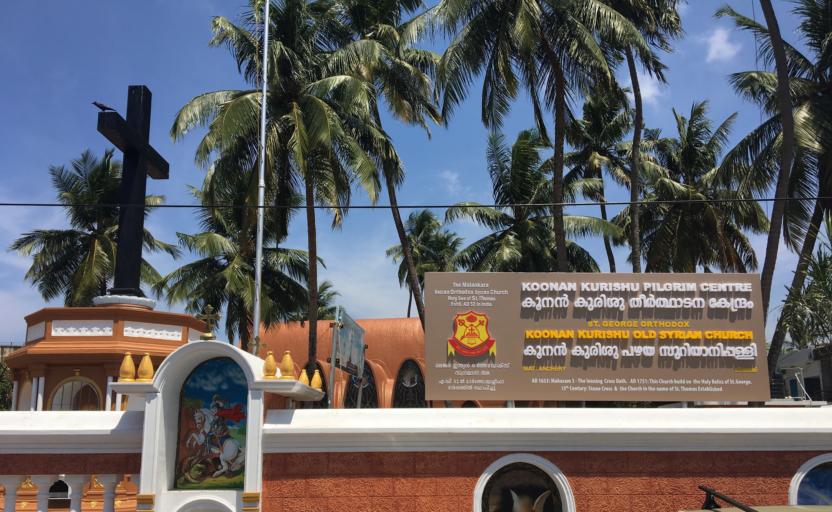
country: IN
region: Kerala
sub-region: Ernakulam
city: Cochin
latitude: 9.9628
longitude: 76.2542
